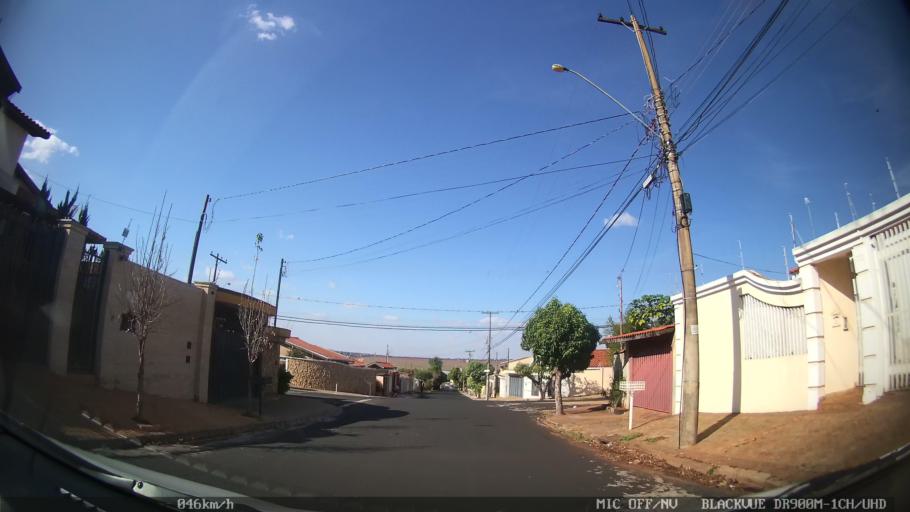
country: BR
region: Sao Paulo
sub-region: Ribeirao Preto
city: Ribeirao Preto
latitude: -21.1755
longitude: -47.7651
